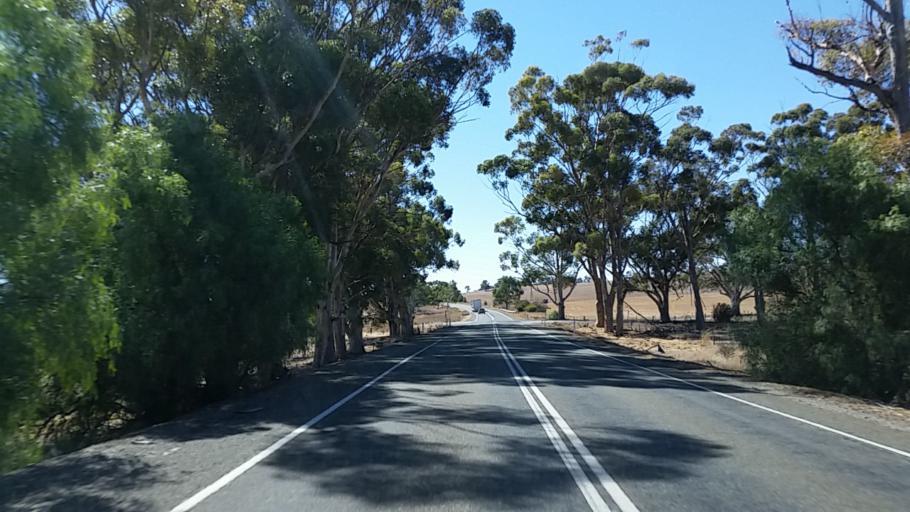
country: AU
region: South Australia
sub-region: Clare and Gilbert Valleys
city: Clare
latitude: -34.0597
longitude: 138.7938
